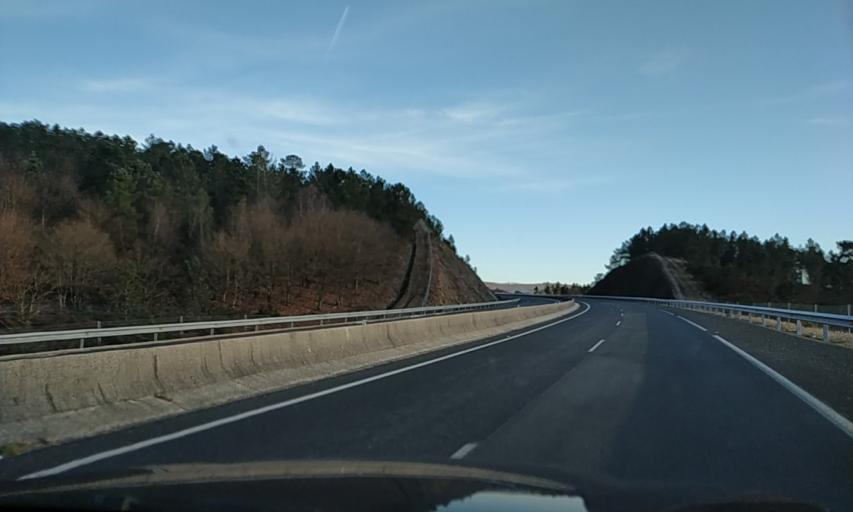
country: ES
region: Galicia
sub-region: Provincia de Pontevedra
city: Lalin
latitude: 42.6051
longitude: -8.0999
